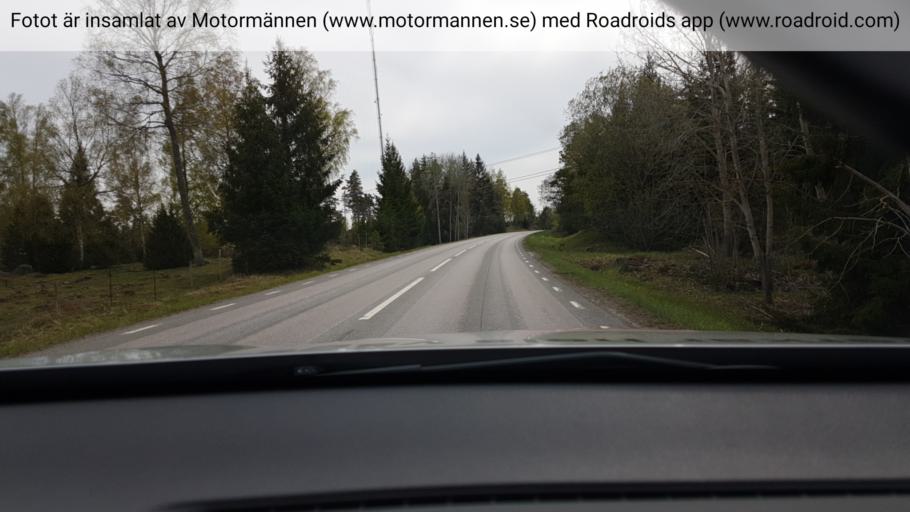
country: SE
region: Stockholm
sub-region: Norrtalje Kommun
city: Nykvarn
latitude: 59.9324
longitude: 18.1198
